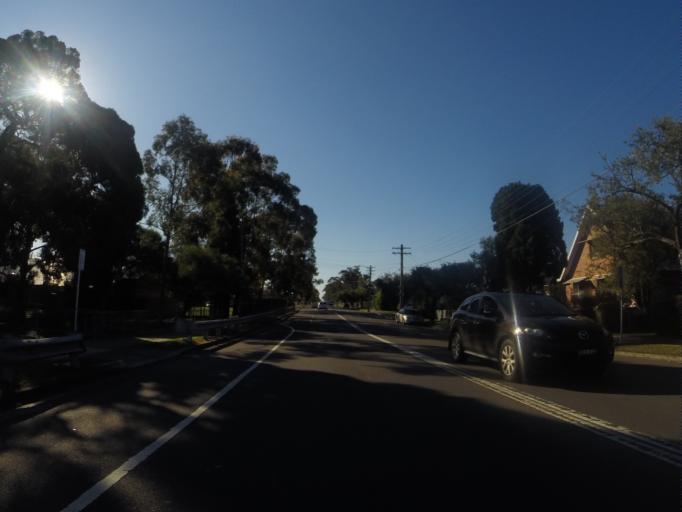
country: AU
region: New South Wales
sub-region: Bankstown
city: Regents Park
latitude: -33.8964
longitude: 151.0211
